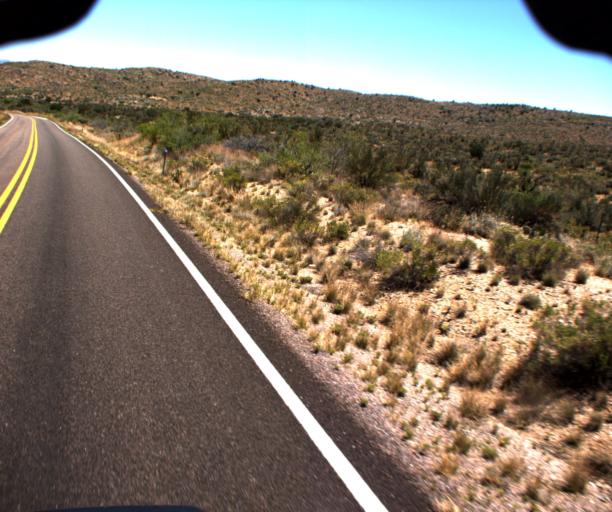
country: US
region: Arizona
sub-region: Yavapai County
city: Bagdad
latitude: 34.5184
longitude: -113.1385
